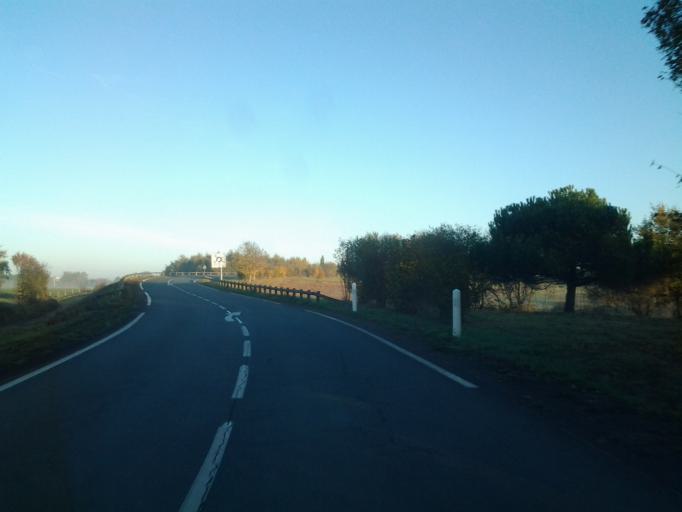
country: FR
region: Pays de la Loire
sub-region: Departement de la Vendee
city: Bournezeau
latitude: 46.6509
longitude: -1.2296
